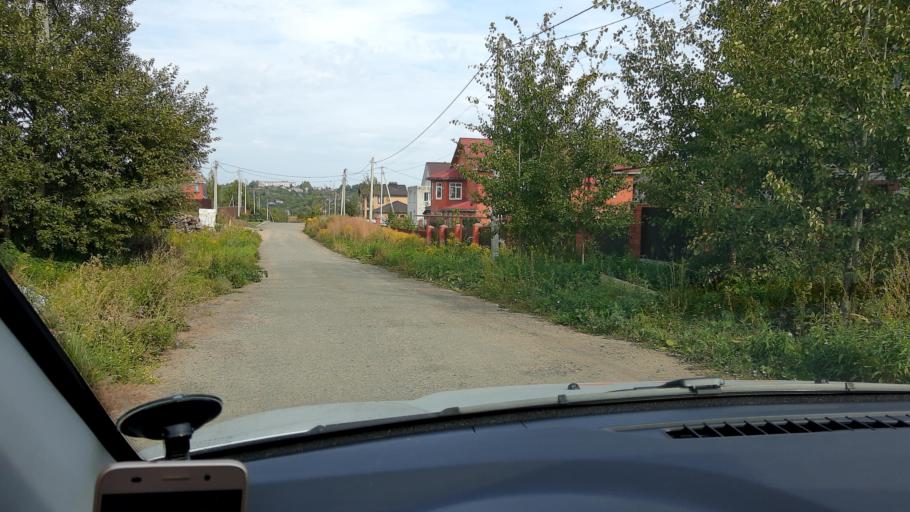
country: RU
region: Nizjnij Novgorod
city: Afonino
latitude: 56.2624
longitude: 44.0657
